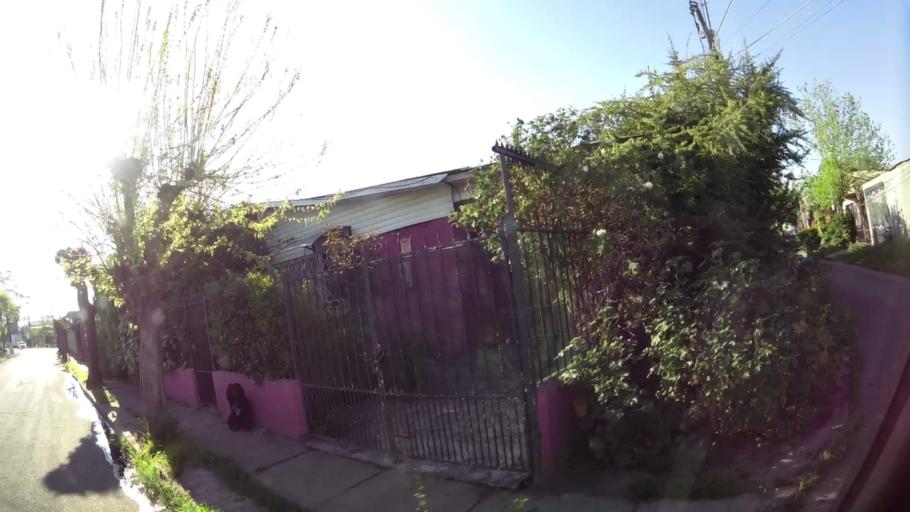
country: CL
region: Santiago Metropolitan
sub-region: Provincia de Santiago
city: Lo Prado
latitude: -33.4881
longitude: -70.7596
